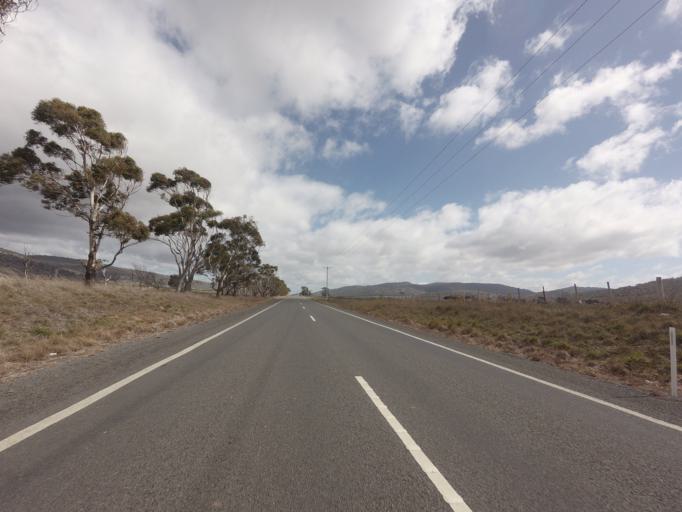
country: AU
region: Tasmania
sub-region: Northern Midlands
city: Evandale
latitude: -41.8098
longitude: 147.6605
